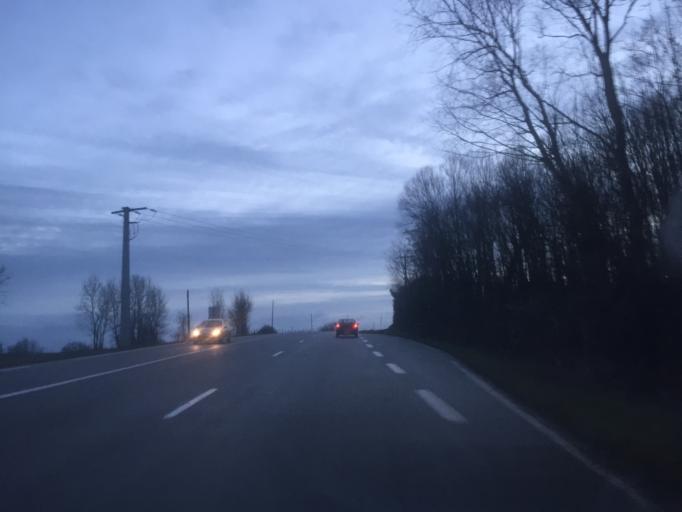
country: FR
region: Franche-Comte
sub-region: Departement du Jura
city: Dole
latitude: 47.1247
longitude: 5.5538
